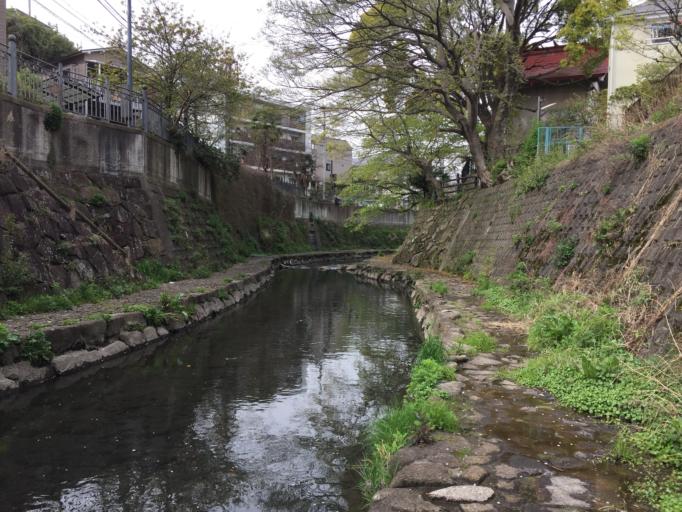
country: JP
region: Kanagawa
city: Yokohama
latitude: 35.4060
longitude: 139.5930
